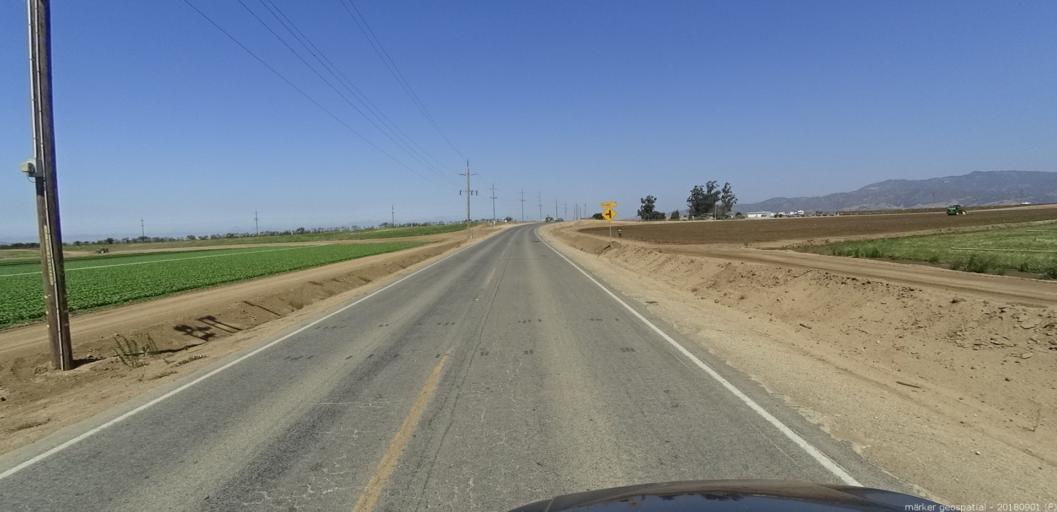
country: US
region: California
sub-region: Monterey County
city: Chualar
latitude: 36.5794
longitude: -121.4966
